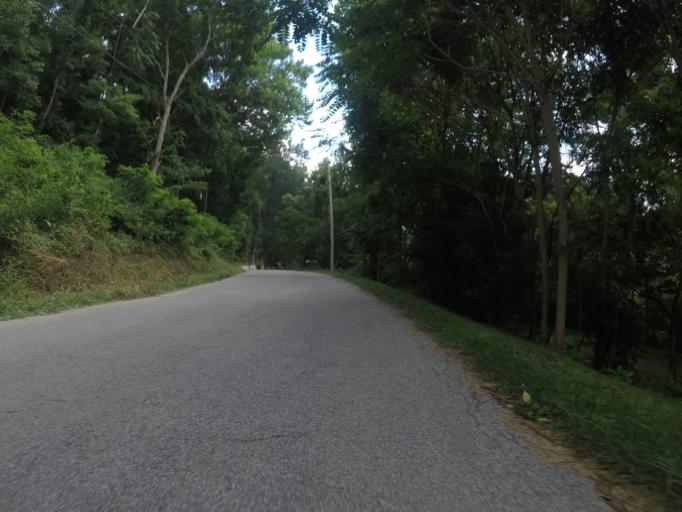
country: US
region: West Virginia
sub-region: Cabell County
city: Pea Ridge
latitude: 38.4213
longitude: -82.3817
